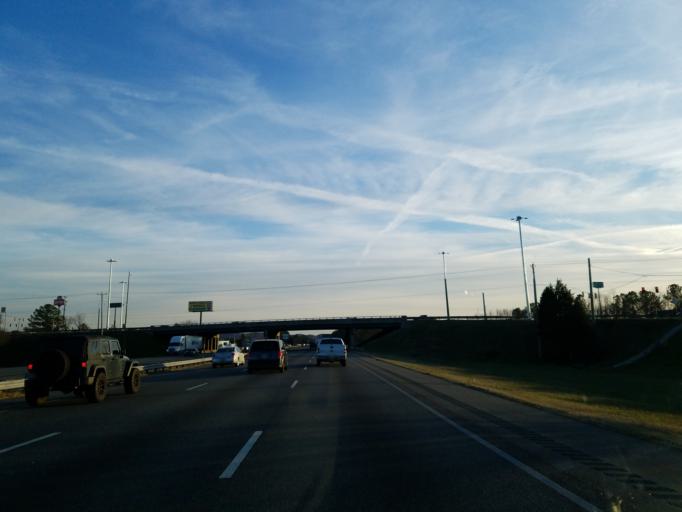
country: US
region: Georgia
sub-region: Gordon County
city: Calhoun
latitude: 34.4726
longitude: -84.9192
